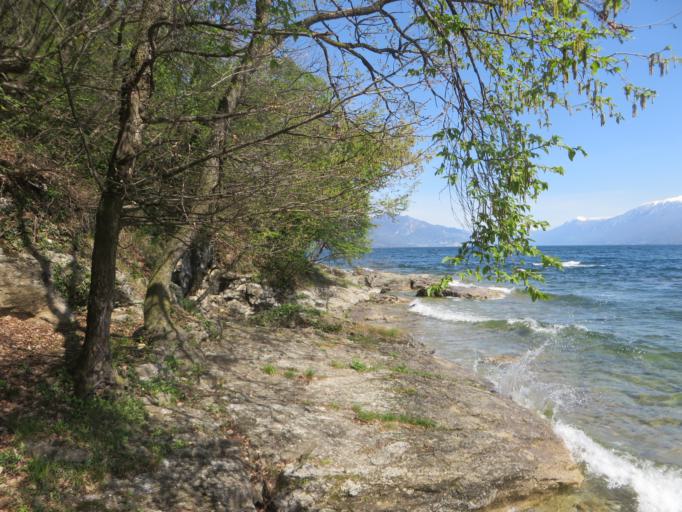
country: IT
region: Lombardy
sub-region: Provincia di Brescia
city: Solarolo
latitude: 45.5526
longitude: 10.5784
